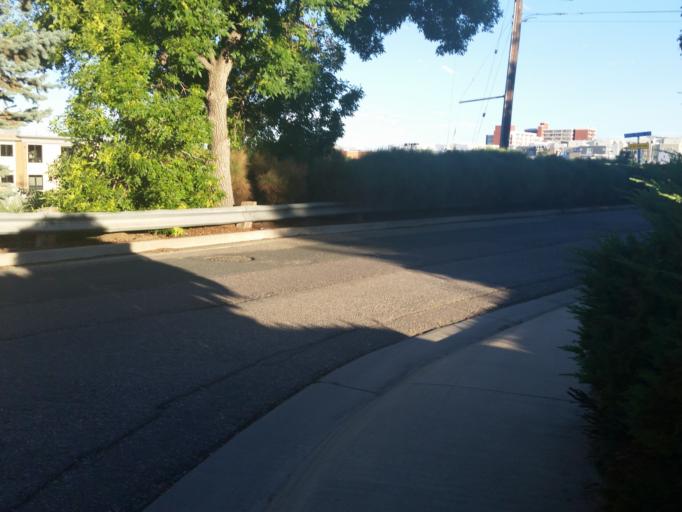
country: US
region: Colorado
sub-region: Boulder County
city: Boulder
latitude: 40.0094
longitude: -105.2591
